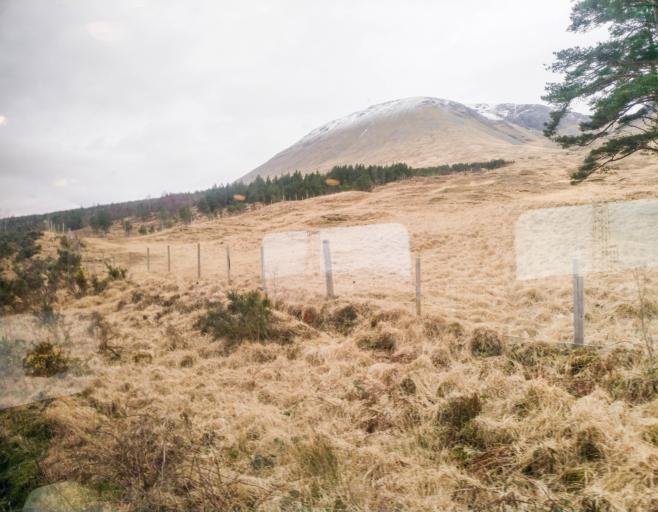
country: GB
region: Scotland
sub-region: Highland
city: Spean Bridge
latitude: 56.5189
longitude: -4.7646
